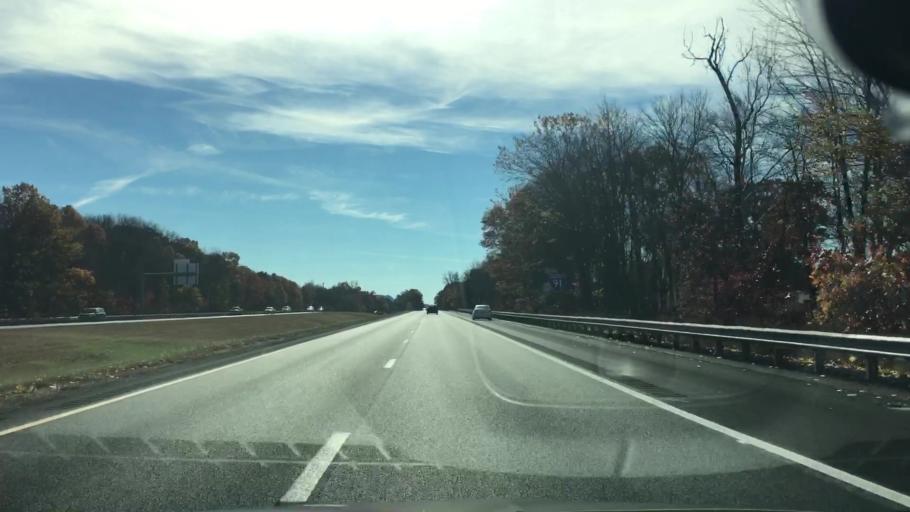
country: US
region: Massachusetts
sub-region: Hampshire County
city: Hatfield
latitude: 42.3921
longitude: -72.6298
